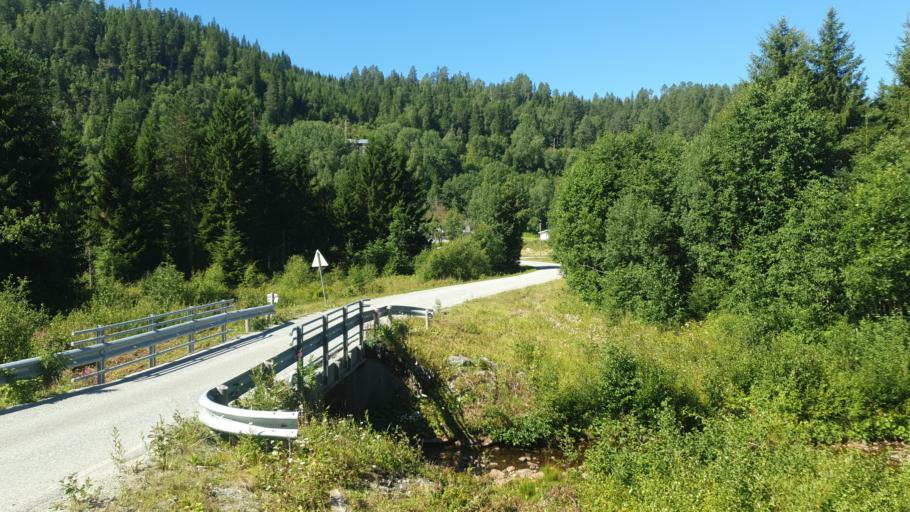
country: NO
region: Sor-Trondelag
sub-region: Meldal
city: Meldal
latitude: 63.1439
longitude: 9.7141
